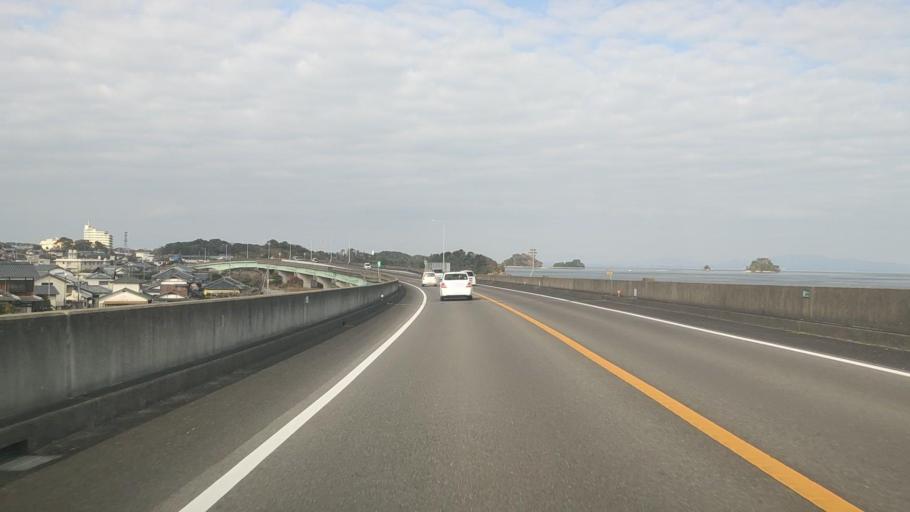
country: JP
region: Nagasaki
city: Shimabara
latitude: 32.7510
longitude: 130.3740
